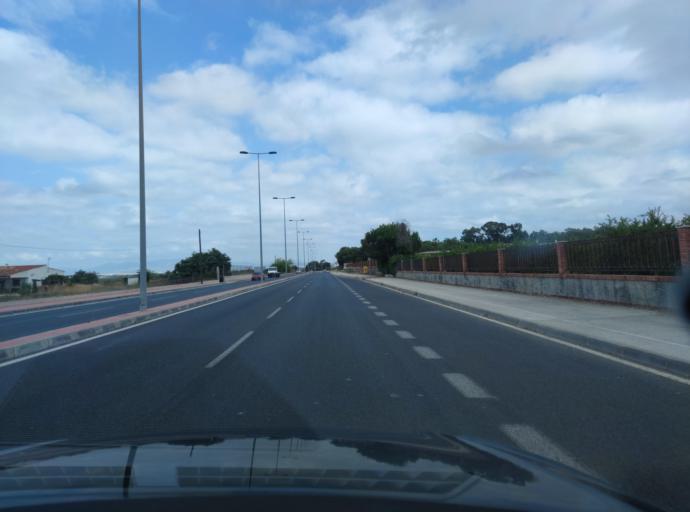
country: ES
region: Valencia
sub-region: Provincia de Alicante
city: Santa Pola
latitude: 38.2073
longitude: -0.5833
